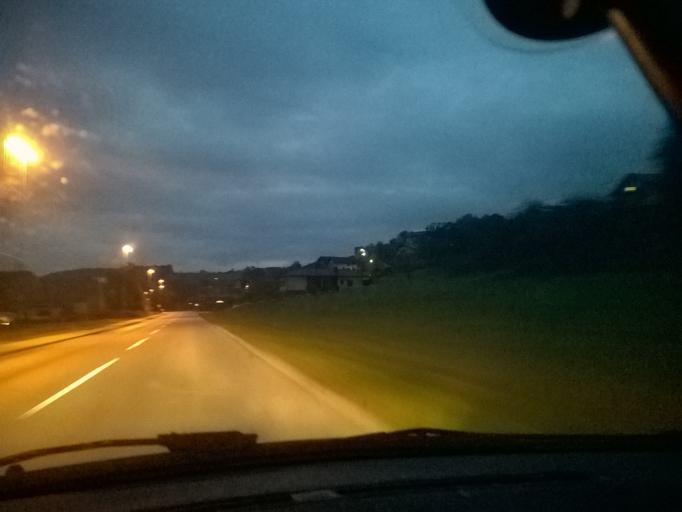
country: SI
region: Rogaska Slatina
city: Rogaska Slatina
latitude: 46.2278
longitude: 15.6478
